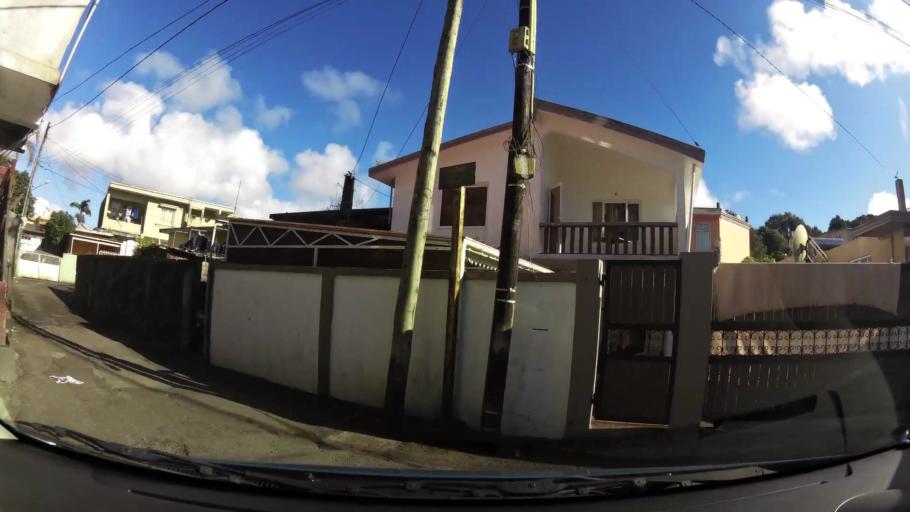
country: MU
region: Plaines Wilhems
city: Curepipe
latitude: -20.3168
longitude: 57.5372
